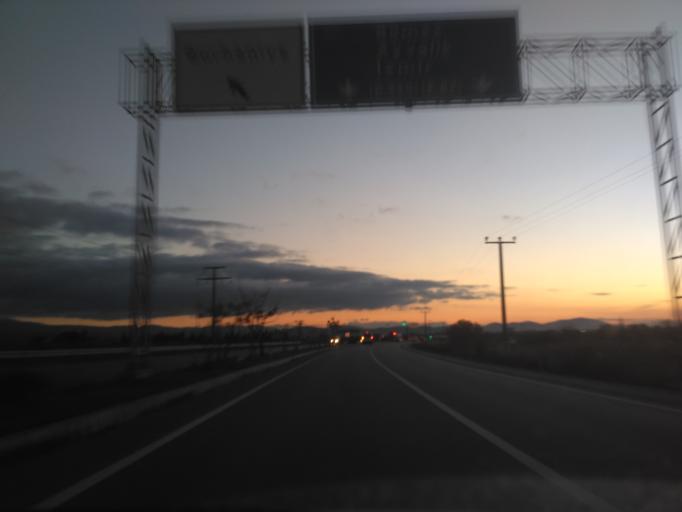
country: TR
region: Balikesir
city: Burhaniye
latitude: 39.5284
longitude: 27.0057
